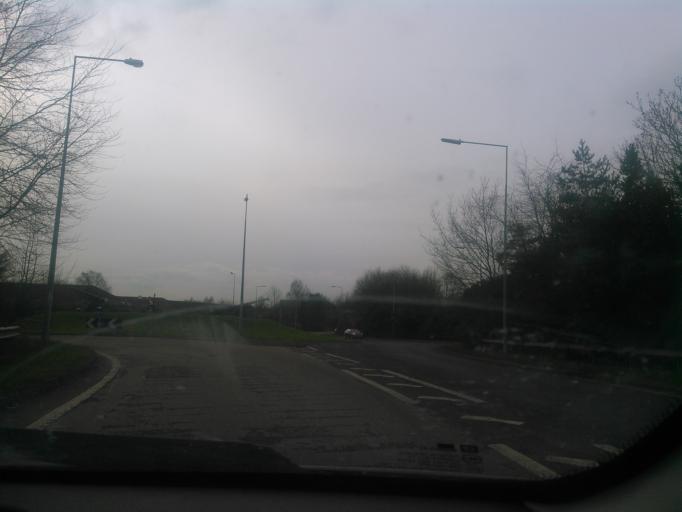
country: GB
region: England
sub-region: Telford and Wrekin
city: Oakengates
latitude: 52.7207
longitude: -2.4429
